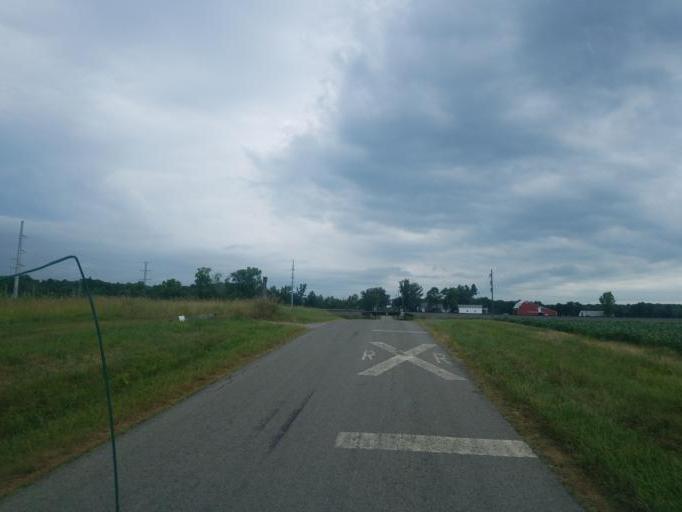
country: US
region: Ohio
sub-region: Defiance County
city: Hicksville
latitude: 41.3027
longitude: -84.8038
